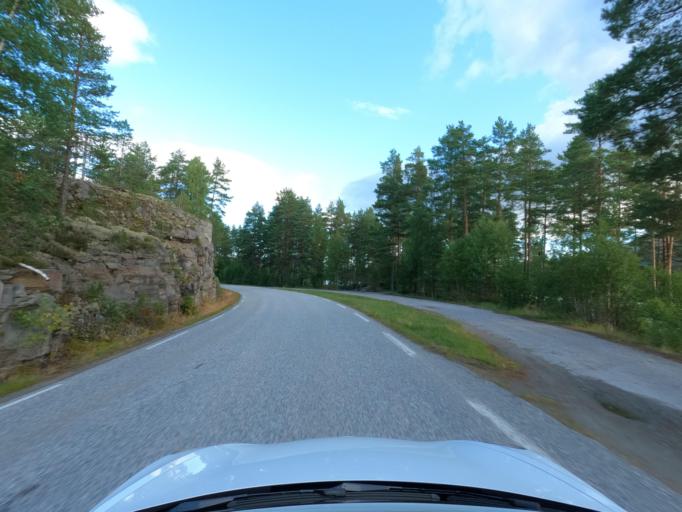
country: NO
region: Telemark
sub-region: Hjartdal
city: Sauland
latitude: 59.7978
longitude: 9.0900
